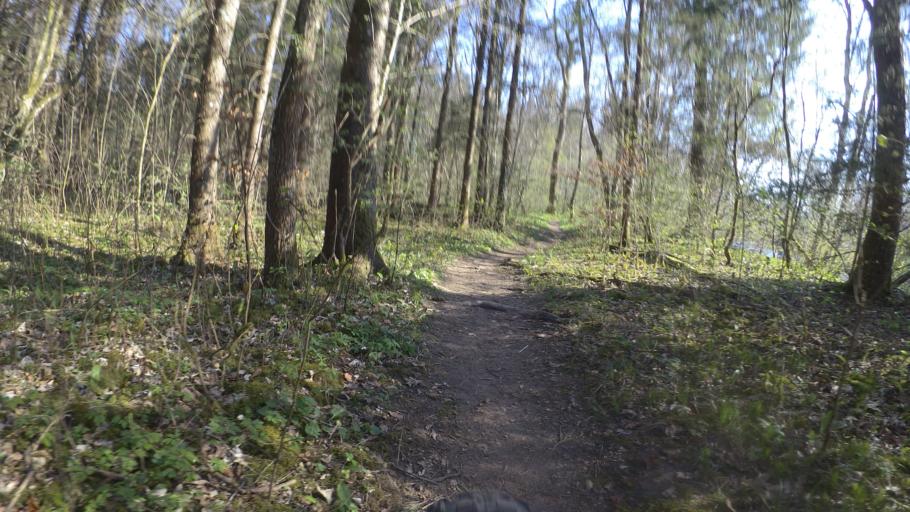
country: DE
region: Bavaria
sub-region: Upper Bavaria
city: Traunreut
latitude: 47.9494
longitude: 12.5869
